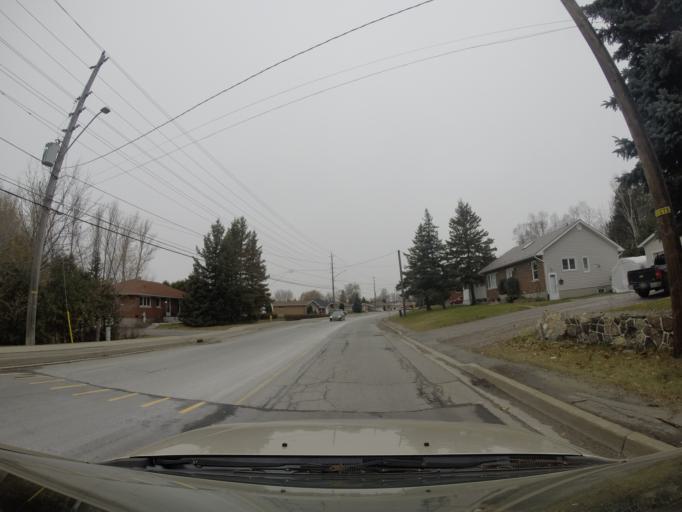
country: CA
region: Ontario
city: Greater Sudbury
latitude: 46.4599
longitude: -81.0199
